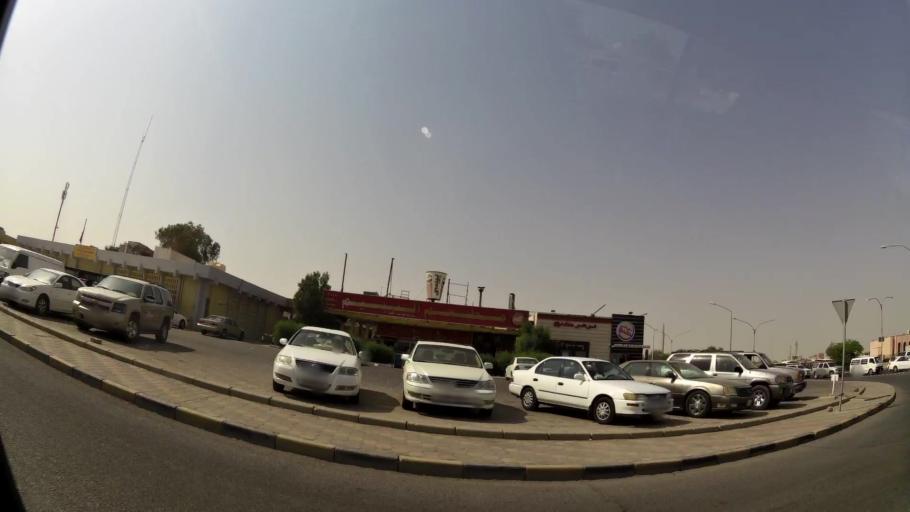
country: KW
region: Muhafazat al Jahra'
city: Al Jahra'
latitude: 29.3284
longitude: 47.6814
